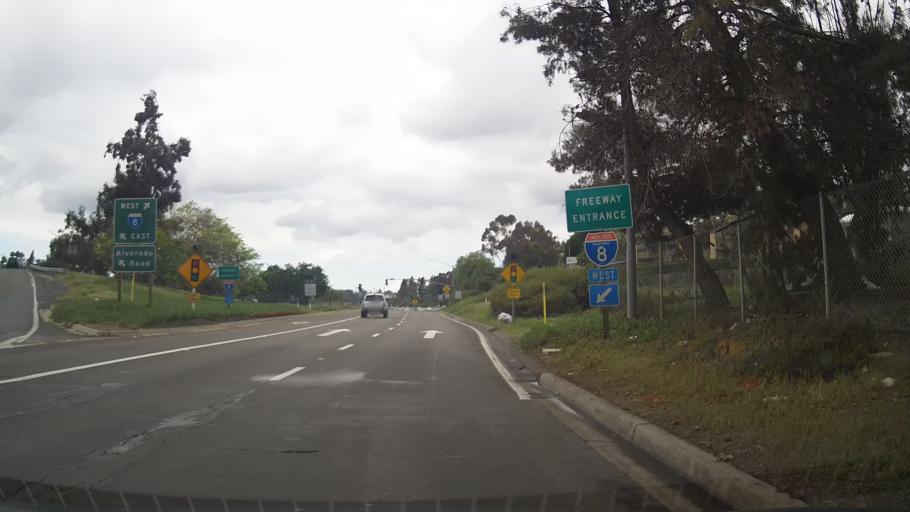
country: US
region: California
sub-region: San Diego County
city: La Mesa
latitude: 32.7740
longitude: -117.0286
